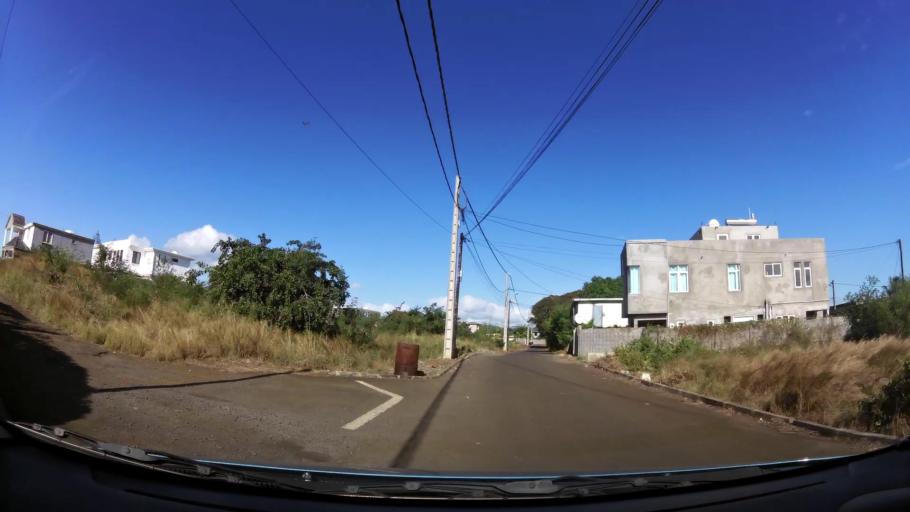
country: MU
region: Black River
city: Albion
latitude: -20.1994
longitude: 57.4104
